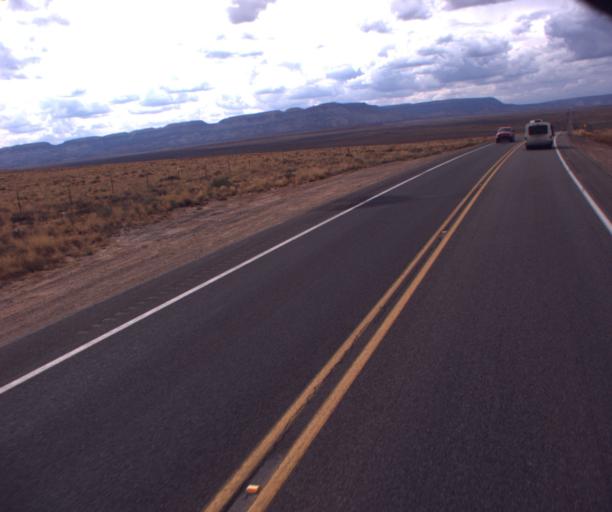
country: US
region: Arizona
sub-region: Navajo County
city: Kayenta
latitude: 36.7292
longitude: -110.1076
